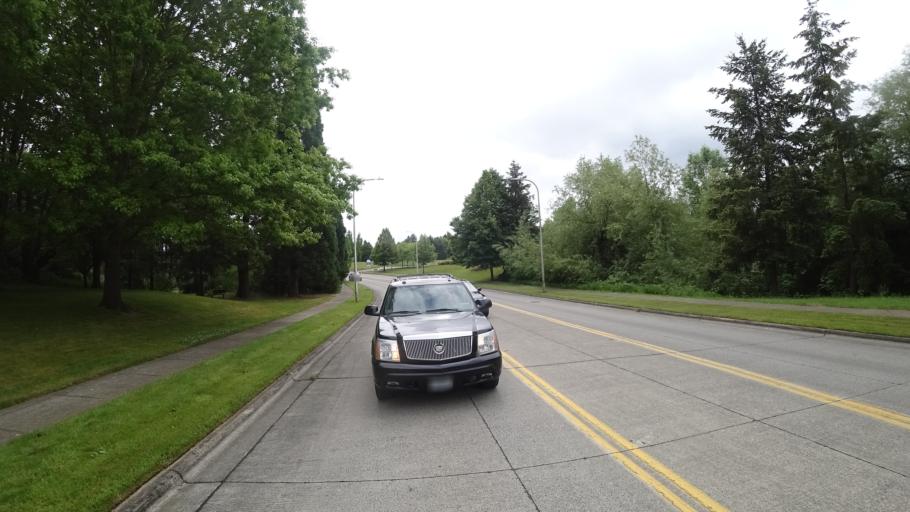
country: US
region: Oregon
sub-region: Washington County
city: Rockcreek
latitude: 45.5347
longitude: -122.8848
